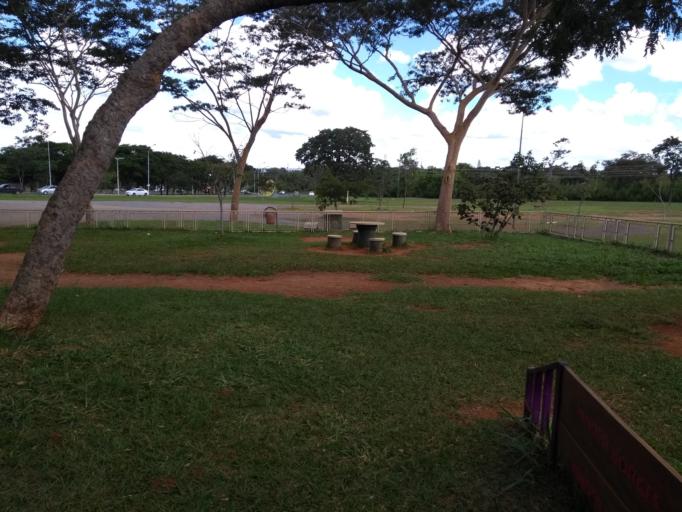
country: BR
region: Federal District
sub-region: Brasilia
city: Brasilia
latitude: -15.8107
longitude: -47.9271
